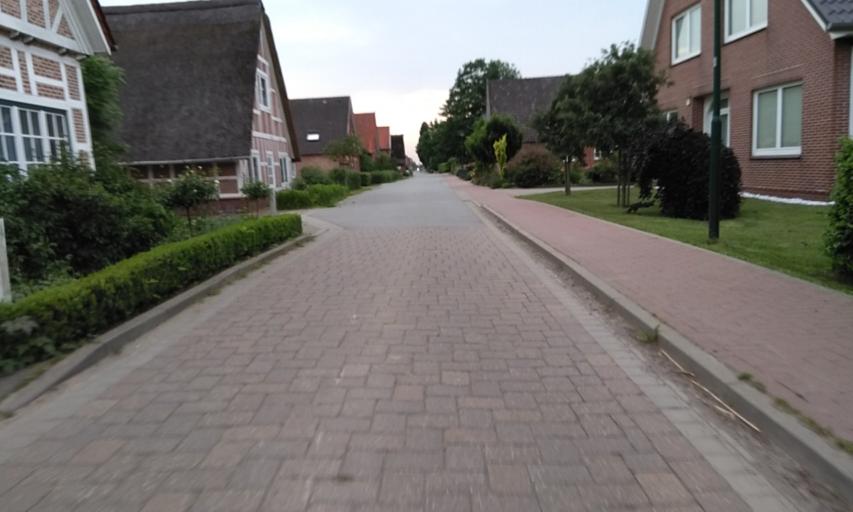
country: DE
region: Lower Saxony
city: Jork
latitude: 53.5175
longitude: 9.6750
